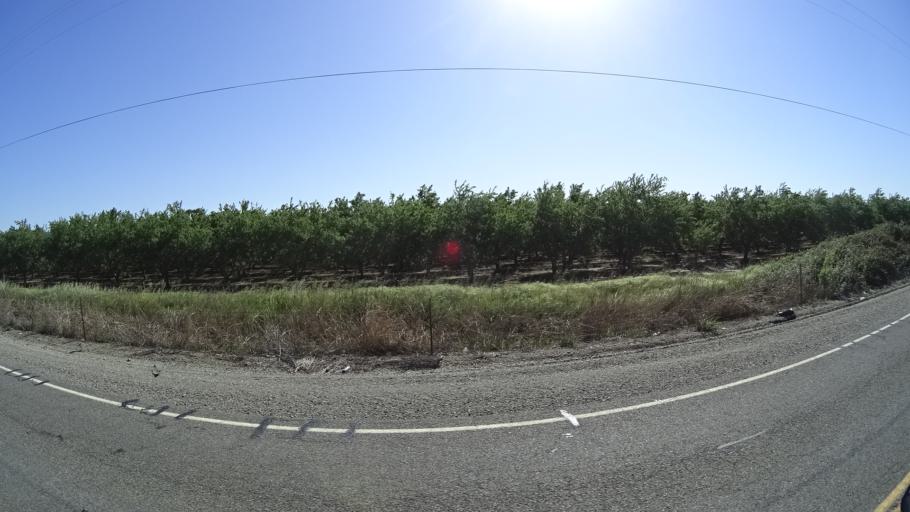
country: US
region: California
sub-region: Glenn County
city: Orland
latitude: 39.7336
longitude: -122.1410
